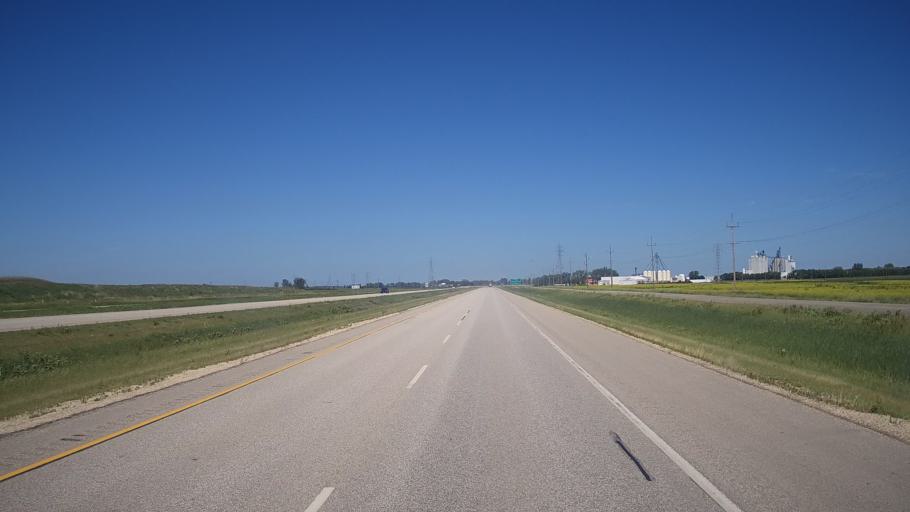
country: CA
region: Manitoba
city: Portage la Prairie
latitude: 49.9576
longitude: -98.3364
